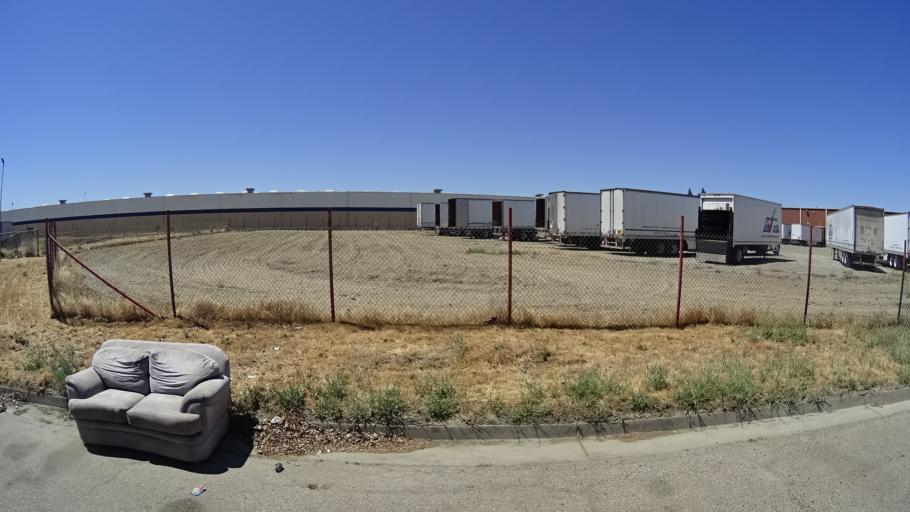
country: US
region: California
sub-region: Fresno County
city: Fresno
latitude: 36.6987
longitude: -119.7706
